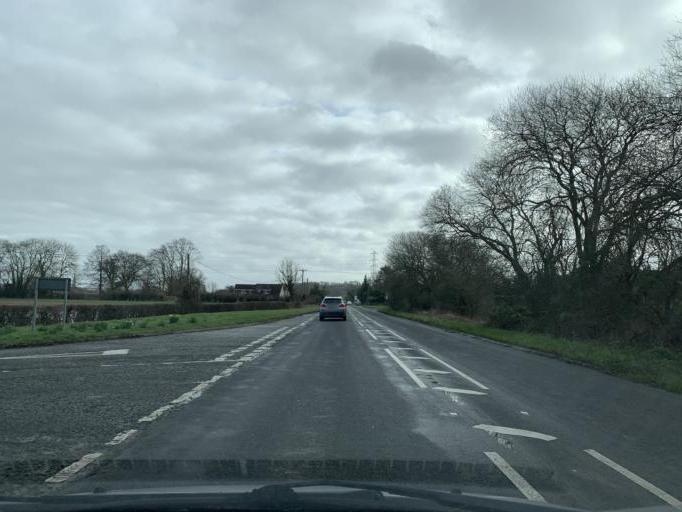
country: GB
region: England
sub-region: Wiltshire
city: Wilton
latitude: 51.0647
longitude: -1.8404
